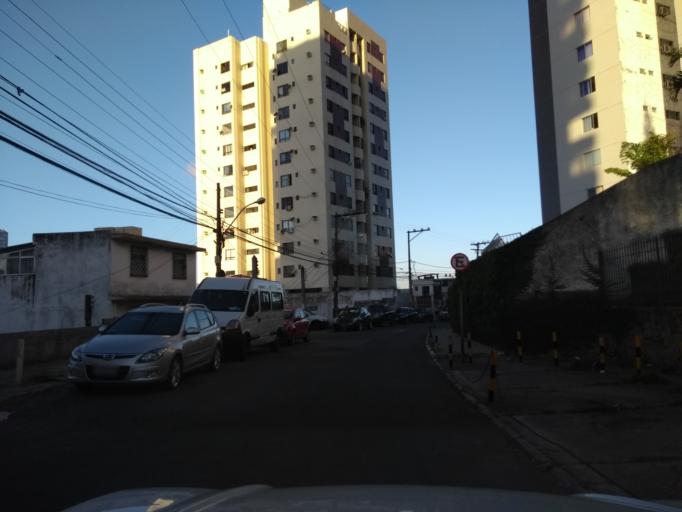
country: BR
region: Bahia
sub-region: Salvador
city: Salvador
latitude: -12.9896
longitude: -38.5138
